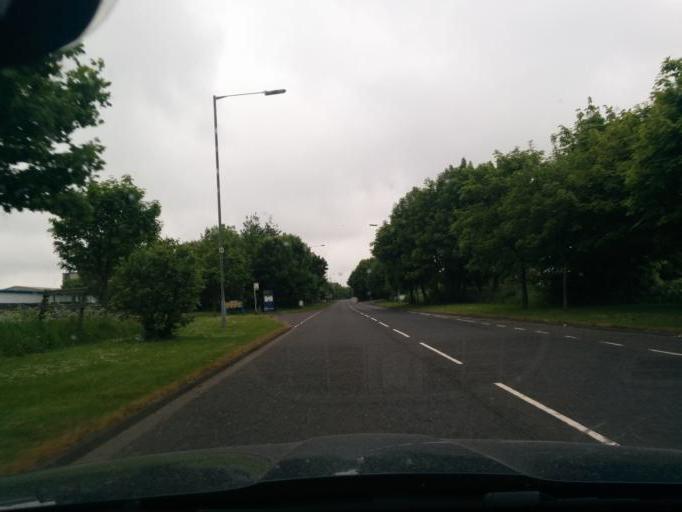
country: GB
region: England
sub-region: Northumberland
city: Cramlington
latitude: 55.0958
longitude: -1.6021
